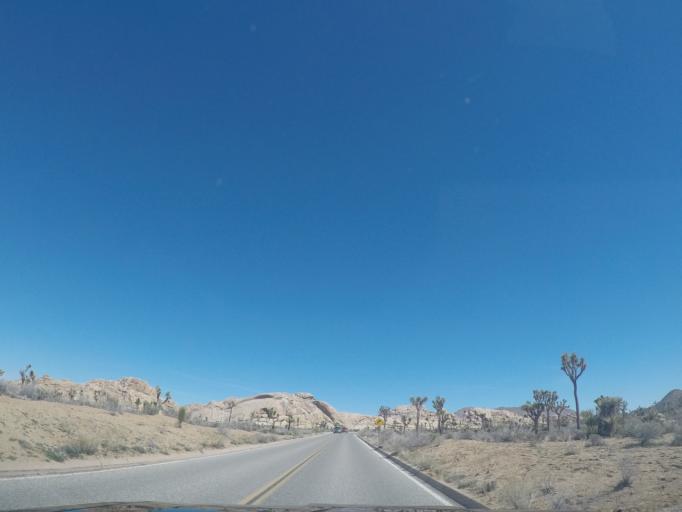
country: US
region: California
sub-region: San Bernardino County
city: Twentynine Palms
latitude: 34.0200
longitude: -116.1578
